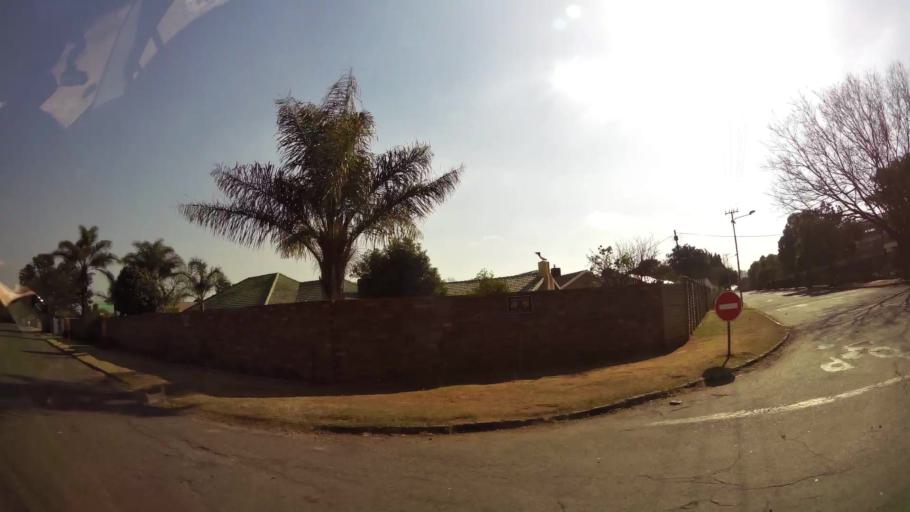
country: ZA
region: Gauteng
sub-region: West Rand District Municipality
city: Randfontein
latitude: -26.1595
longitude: 27.7048
